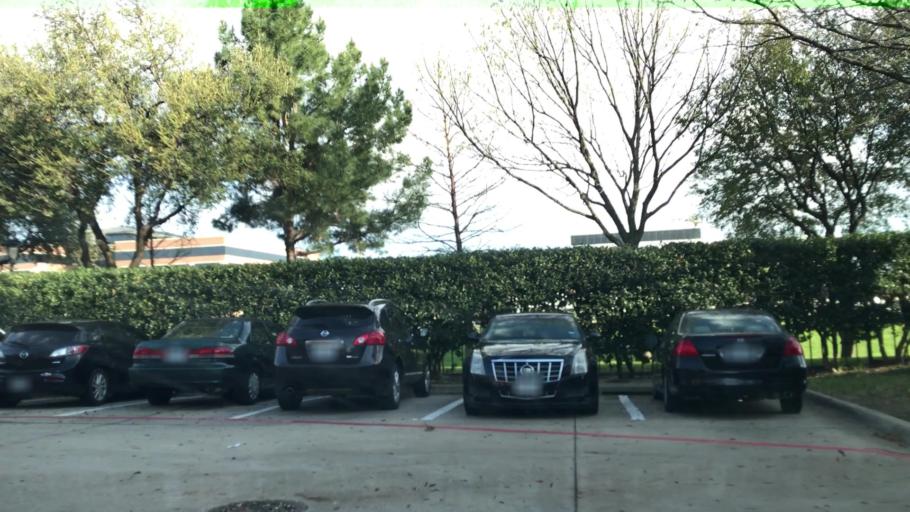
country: US
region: Texas
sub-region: Dallas County
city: Coppell
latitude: 32.9008
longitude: -96.9662
